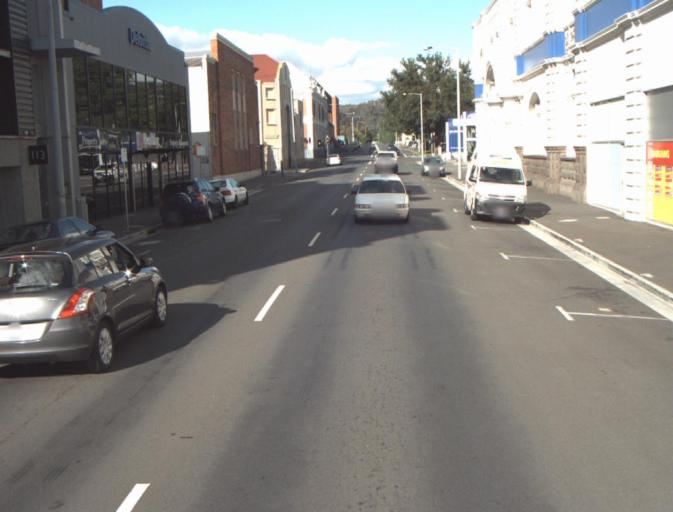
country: AU
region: Tasmania
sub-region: Launceston
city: Launceston
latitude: -41.4341
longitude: 147.1382
